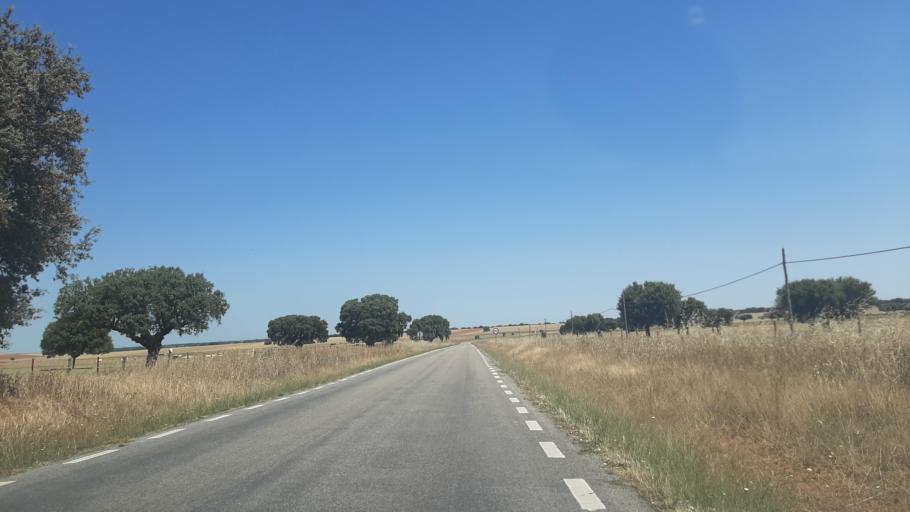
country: ES
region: Castille and Leon
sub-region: Provincia de Salamanca
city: Cabrillas
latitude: 40.7119
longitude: -6.1786
